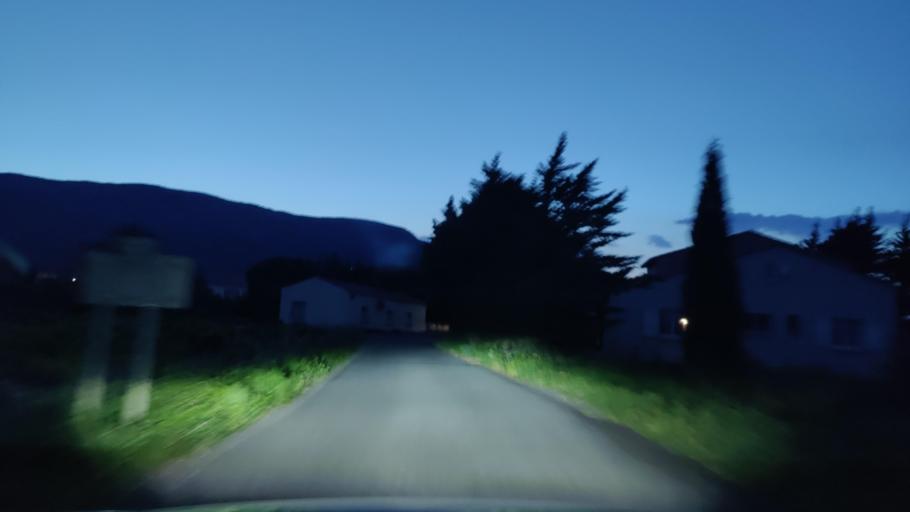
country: FR
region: Languedoc-Roussillon
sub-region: Departement des Pyrenees-Orientales
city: Estagel
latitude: 42.8861
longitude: 2.7268
